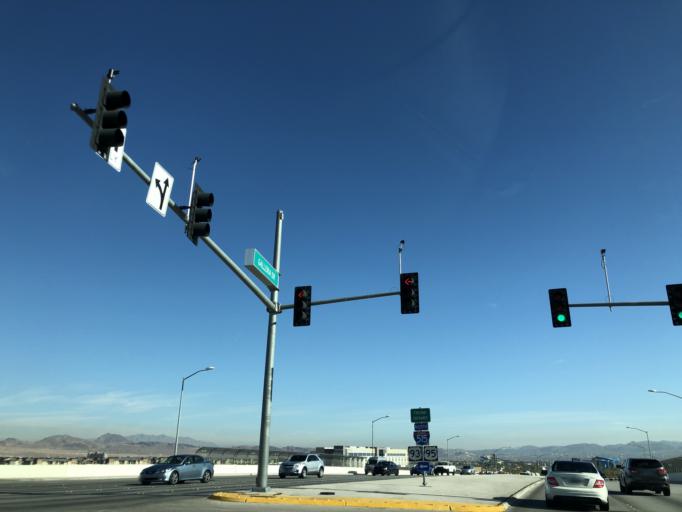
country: US
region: Nevada
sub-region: Clark County
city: Whitney
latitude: 36.0722
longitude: -115.0349
